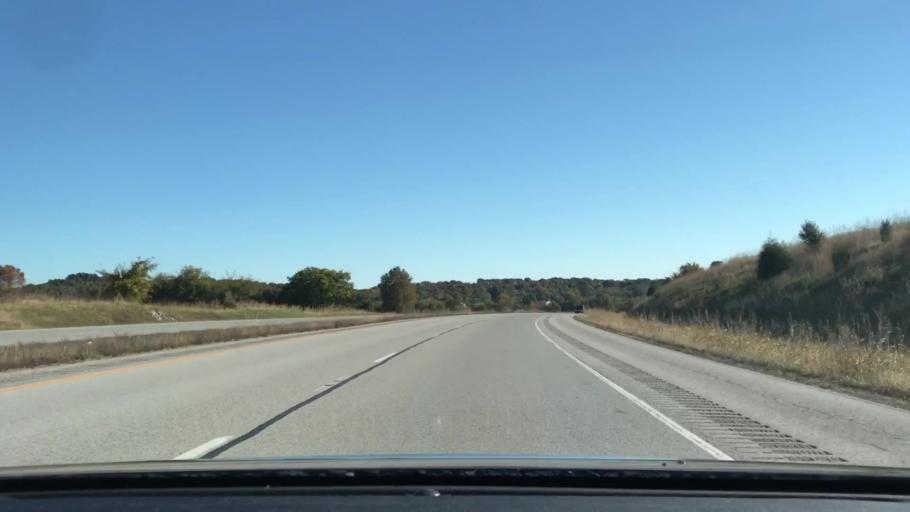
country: US
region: Kentucky
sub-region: Logan County
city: Auburn
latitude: 36.8911
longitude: -86.6532
